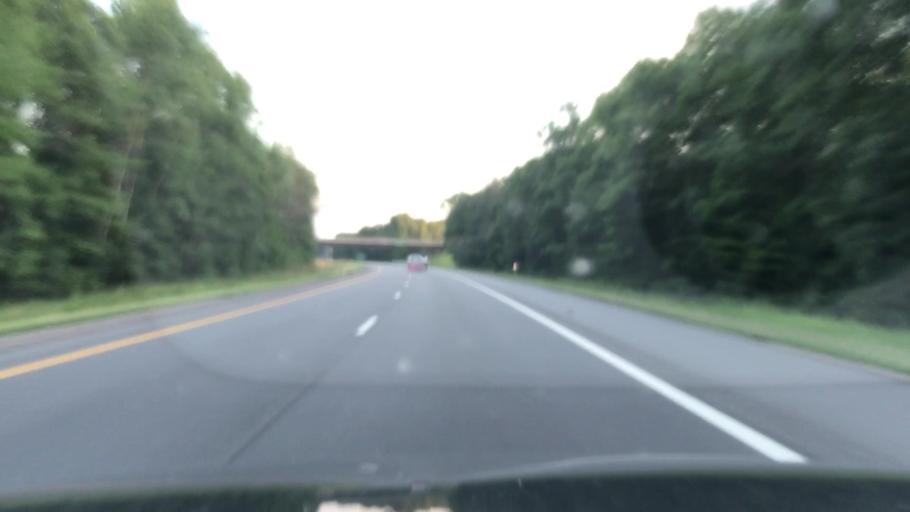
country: US
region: Michigan
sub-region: Montcalm County
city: Howard City
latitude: 43.4417
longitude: -85.4927
